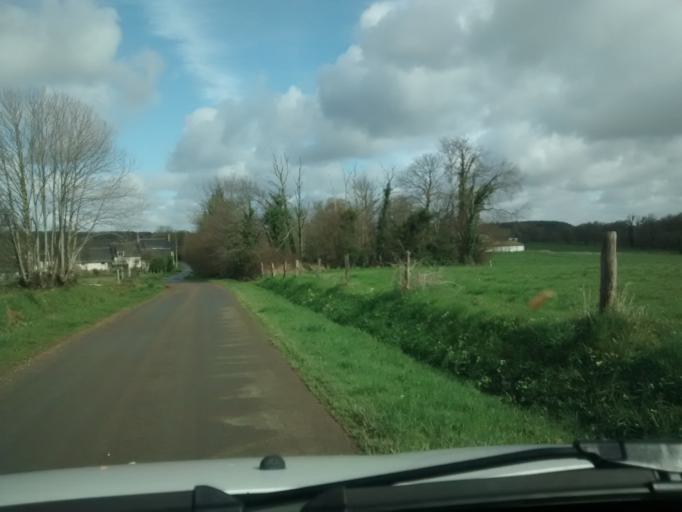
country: FR
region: Brittany
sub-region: Departement d'Ille-et-Vilaine
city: Liffre
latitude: 48.1719
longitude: -1.5150
